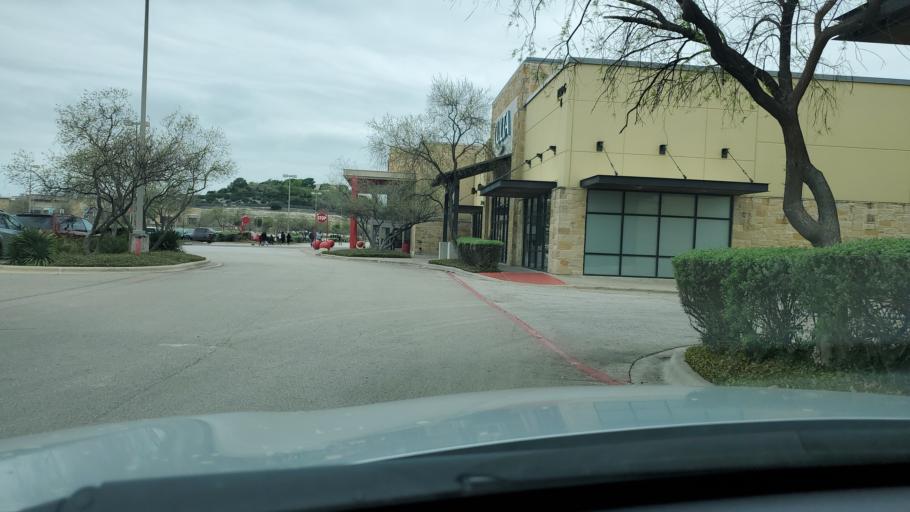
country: US
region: Texas
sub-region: Bell County
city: Harker Heights
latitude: 31.0737
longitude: -97.6617
